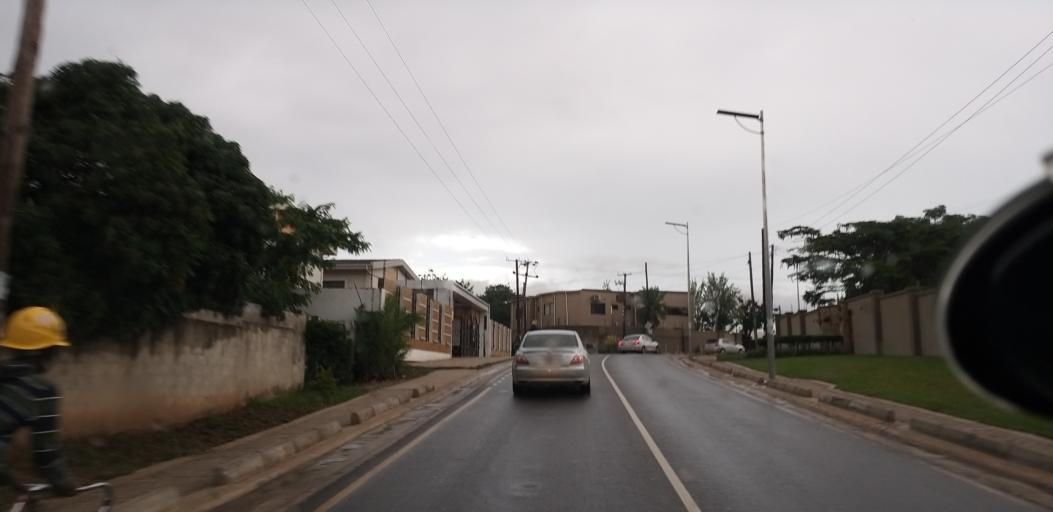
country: ZM
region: Lusaka
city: Lusaka
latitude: -15.4160
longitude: 28.3628
